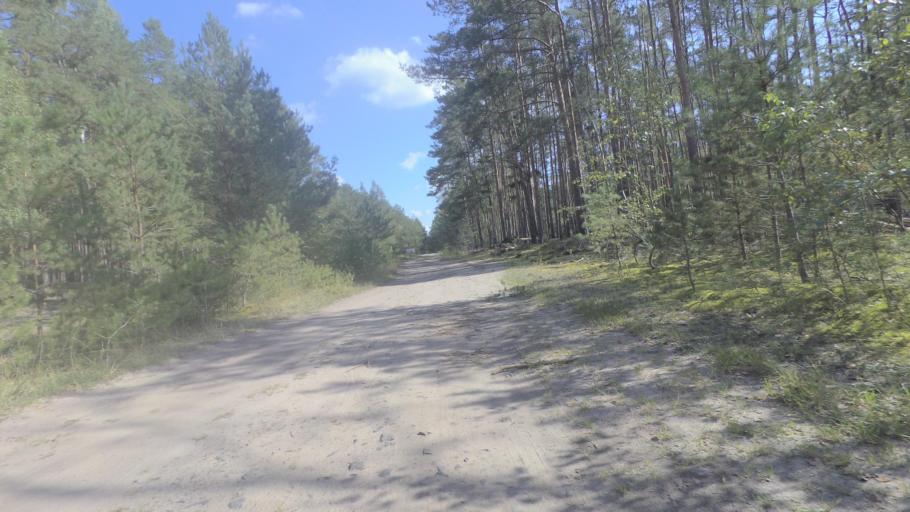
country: DE
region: Brandenburg
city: Halbe
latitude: 52.1505
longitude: 13.7170
